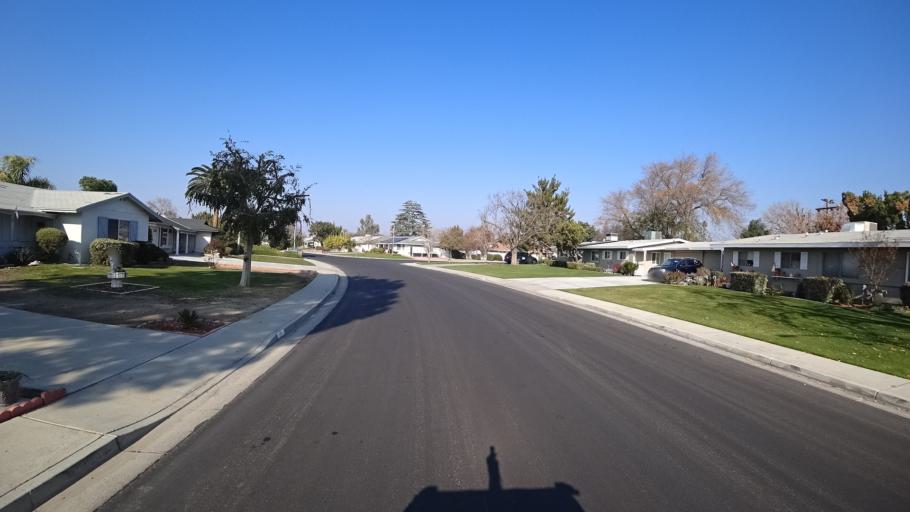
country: US
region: California
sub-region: Kern County
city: Greenacres
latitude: 35.3477
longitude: -119.0710
